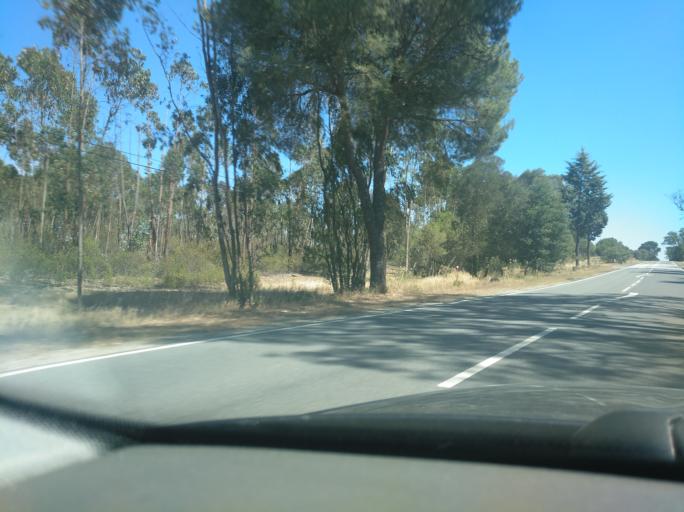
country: PT
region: Beja
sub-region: Almodovar
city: Almodovar
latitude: 37.5928
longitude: -8.0803
